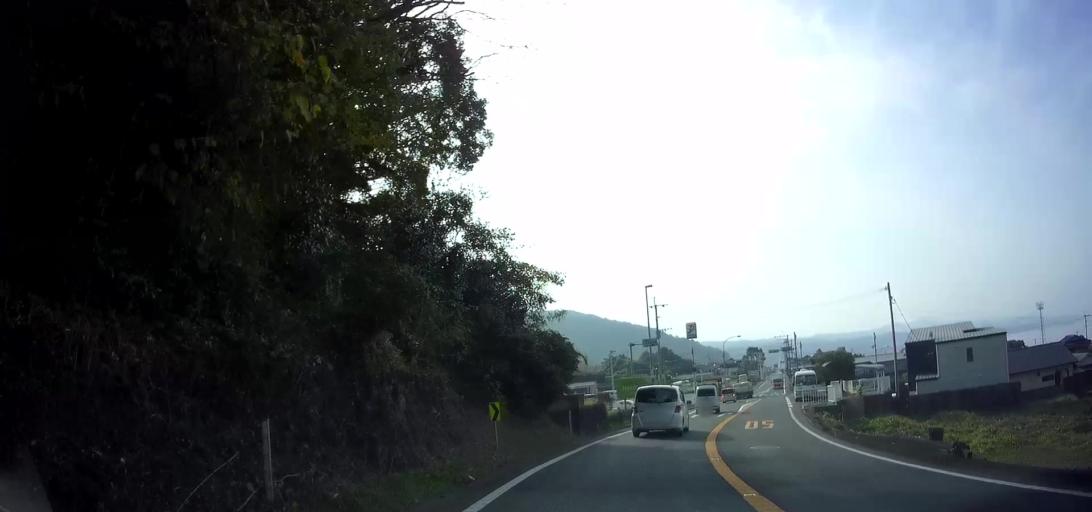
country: JP
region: Nagasaki
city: Shimabara
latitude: 32.7519
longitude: 130.2113
